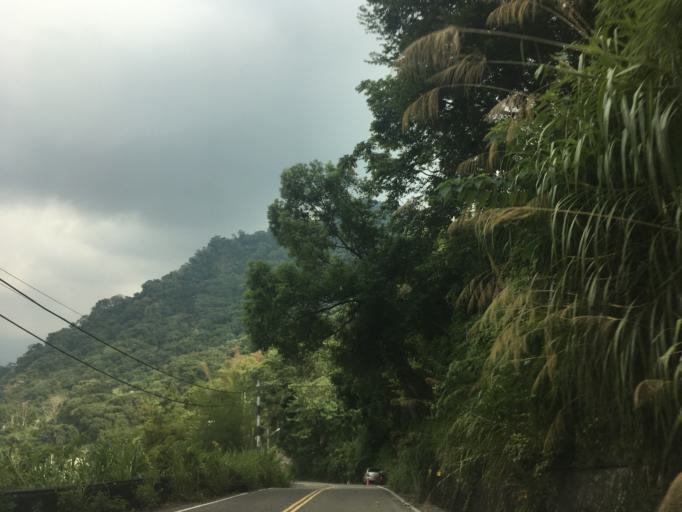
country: TW
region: Taiwan
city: Fengyuan
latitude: 24.3358
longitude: 120.9297
